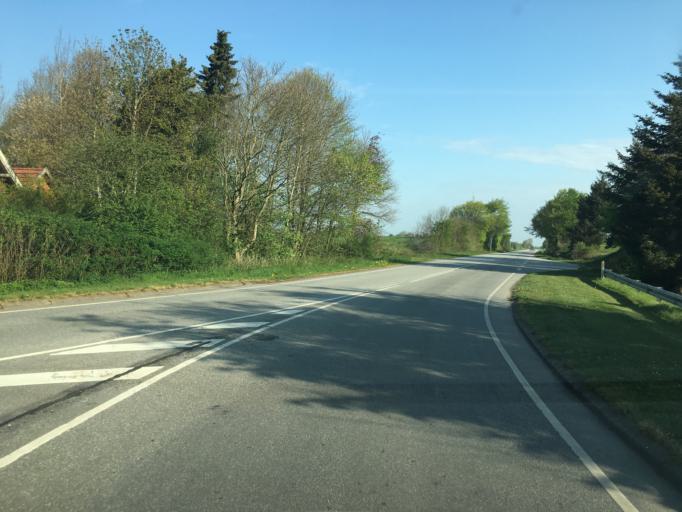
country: DK
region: South Denmark
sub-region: Aabenraa Kommune
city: Aabenraa
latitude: 55.0819
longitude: 9.3830
